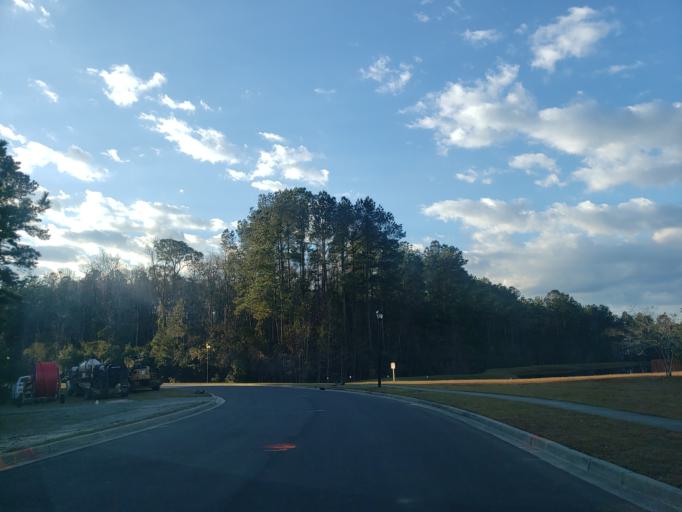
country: US
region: Georgia
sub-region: Chatham County
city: Bloomingdale
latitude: 32.1573
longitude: -81.2658
